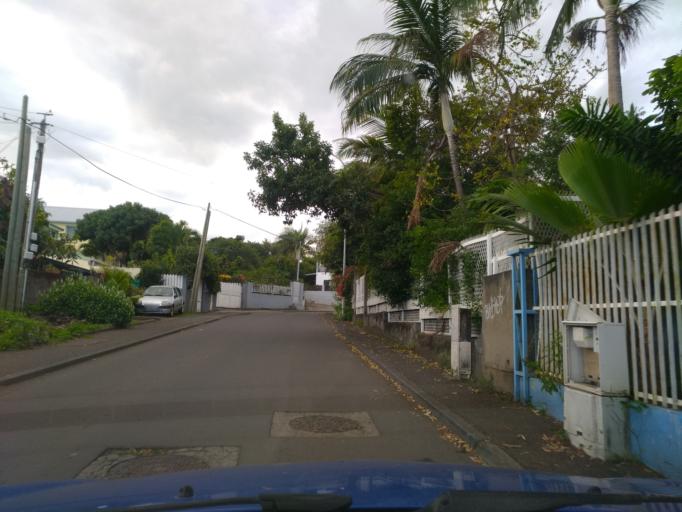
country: RE
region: Reunion
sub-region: Reunion
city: Saint-Pierre
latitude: -21.3298
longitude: 55.4776
